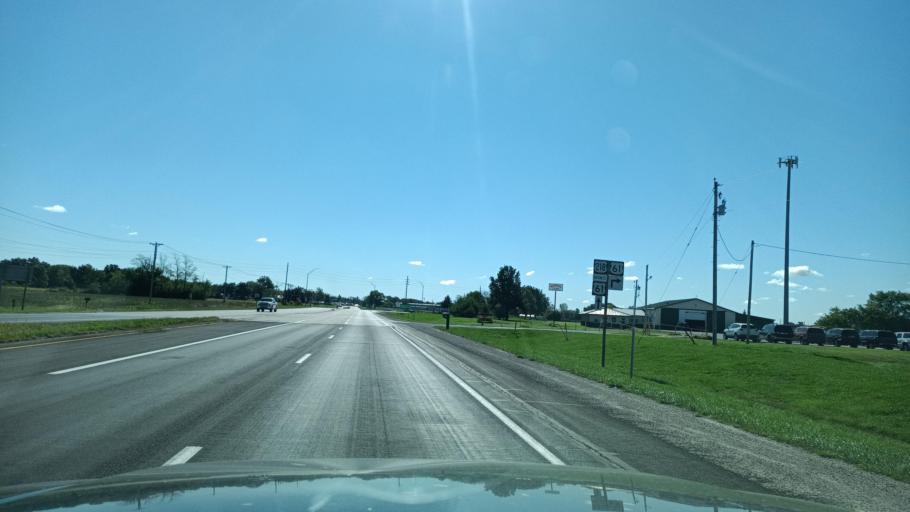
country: US
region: Iowa
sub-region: Lee County
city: Keokuk
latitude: 40.4381
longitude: -91.4287
